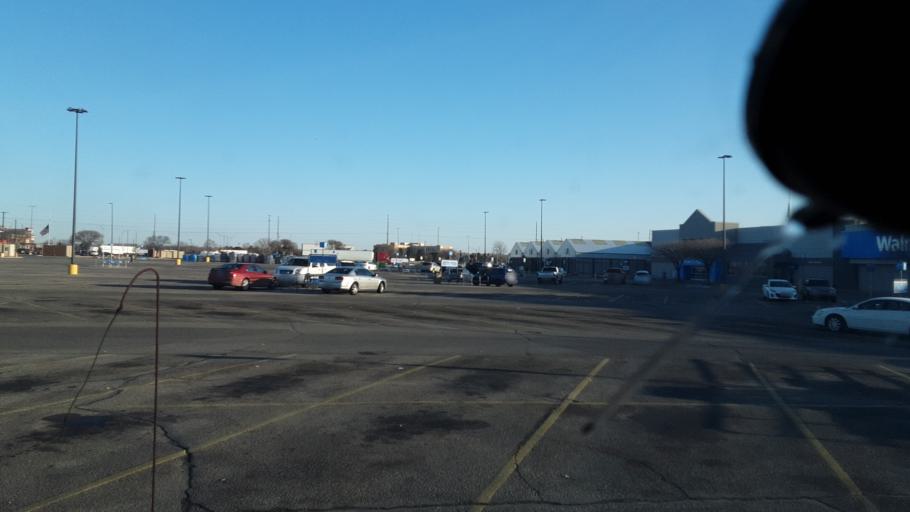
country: US
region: Kansas
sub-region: Reno County
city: Hutchinson
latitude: 38.0695
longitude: -97.8937
